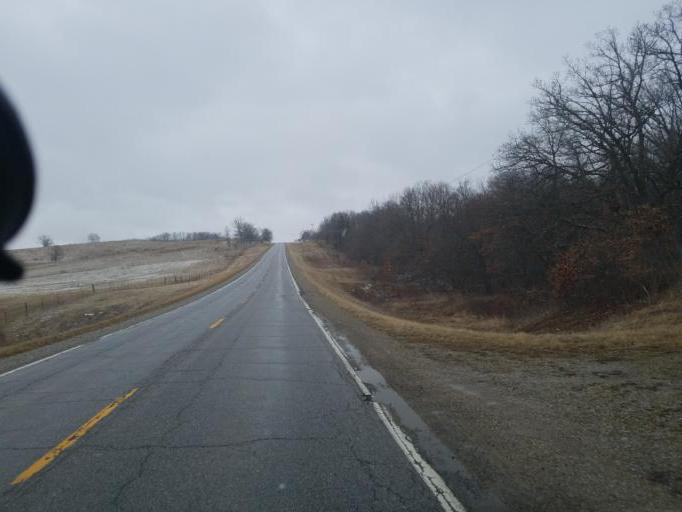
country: US
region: Missouri
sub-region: Putnam County
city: Unionville
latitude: 40.5285
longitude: -93.0155
